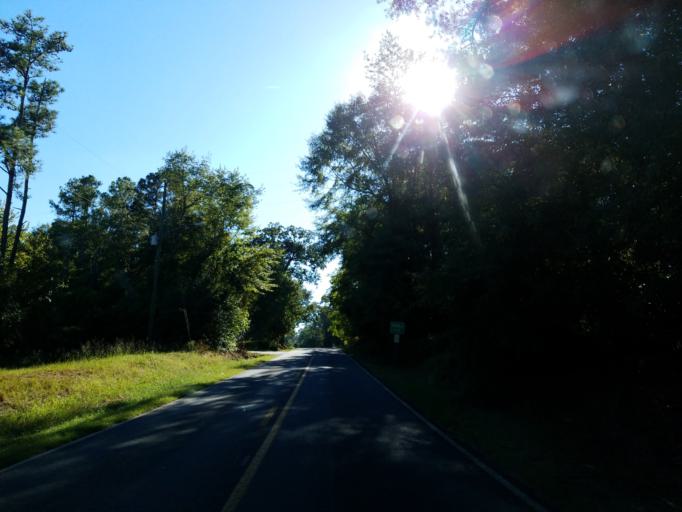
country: US
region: Georgia
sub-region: Dooly County
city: Vienna
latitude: 32.2045
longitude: -83.9019
